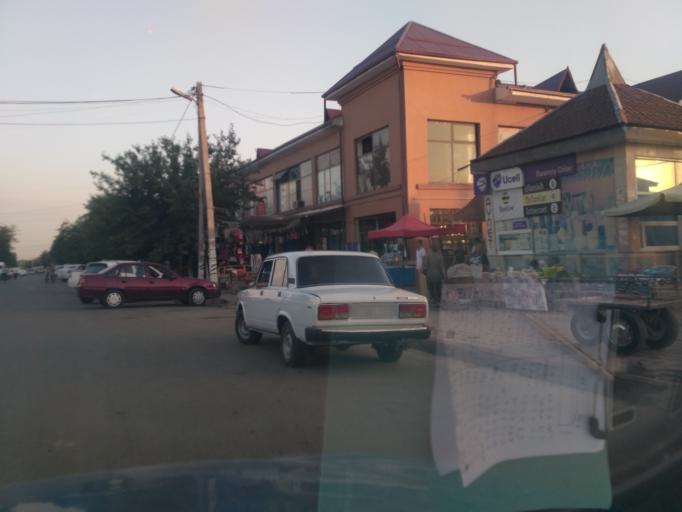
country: UZ
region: Sirdaryo
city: Guliston
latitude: 40.4939
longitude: 68.7667
